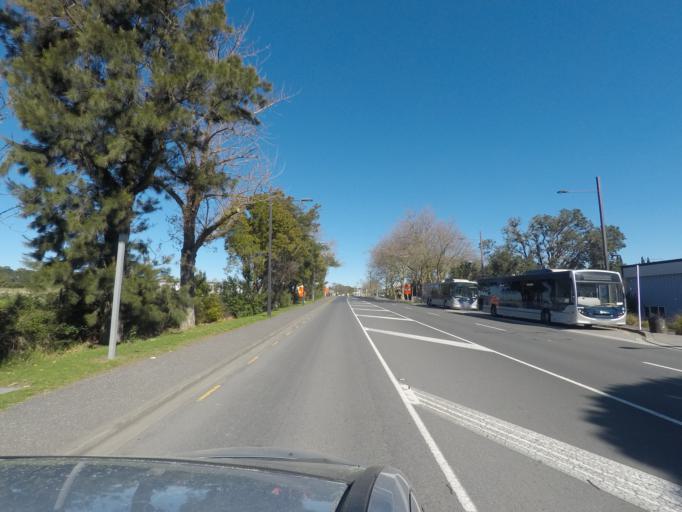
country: NZ
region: Auckland
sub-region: Auckland
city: Waitakere
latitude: -36.9110
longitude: 174.6828
